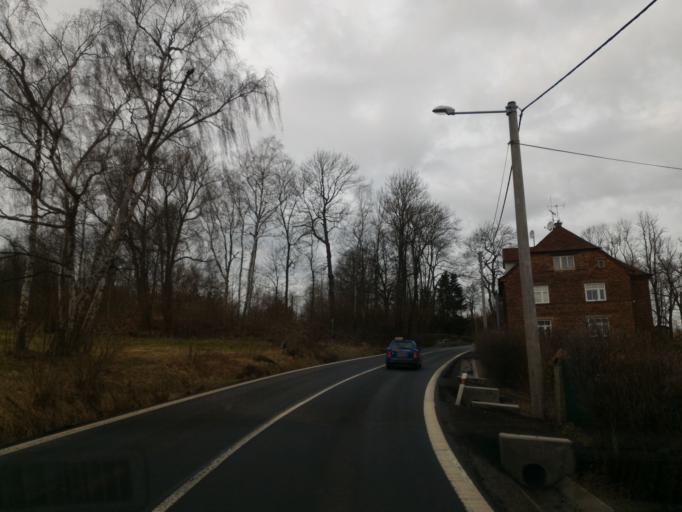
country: CZ
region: Ustecky
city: Dolni Podluzi
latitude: 50.9077
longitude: 14.5734
